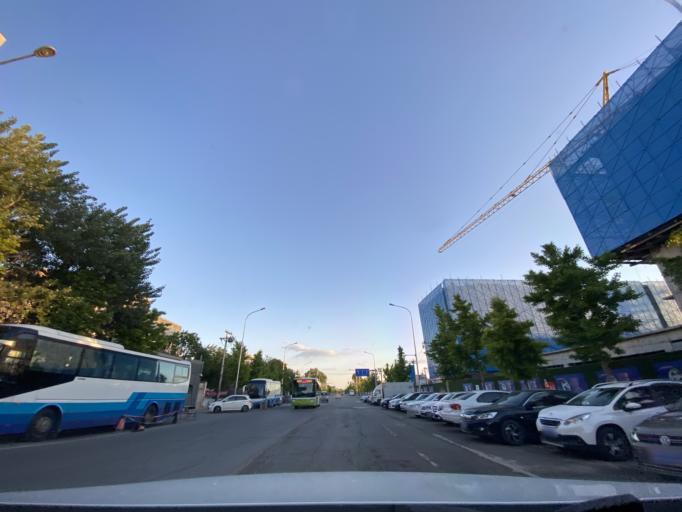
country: CN
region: Beijing
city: Sijiqing
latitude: 39.9539
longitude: 116.2632
